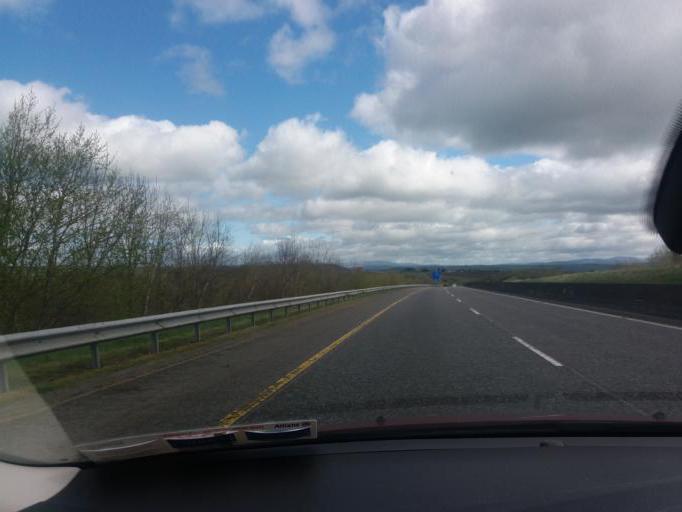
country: IE
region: Munster
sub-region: County Cork
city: Watergrasshill
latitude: 52.0428
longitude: -8.3139
